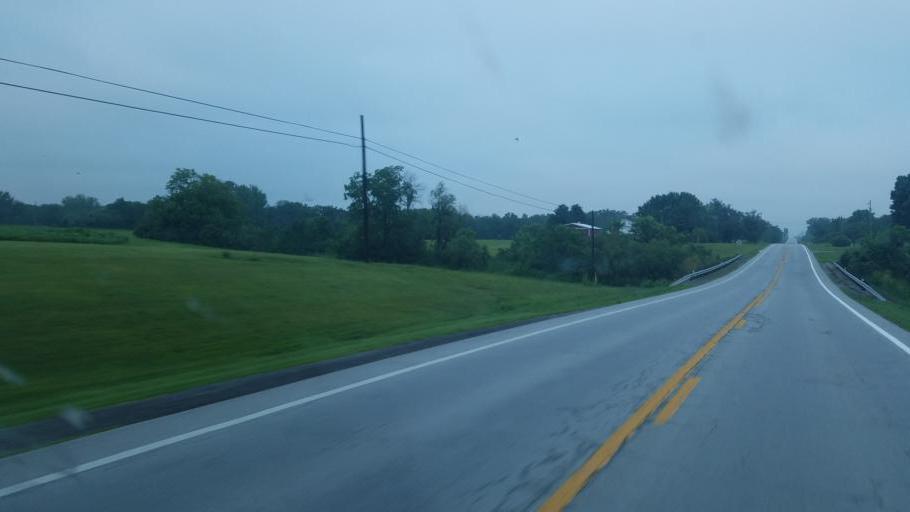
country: US
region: Ohio
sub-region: Madison County
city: Mount Sterling
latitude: 39.6803
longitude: -83.3024
